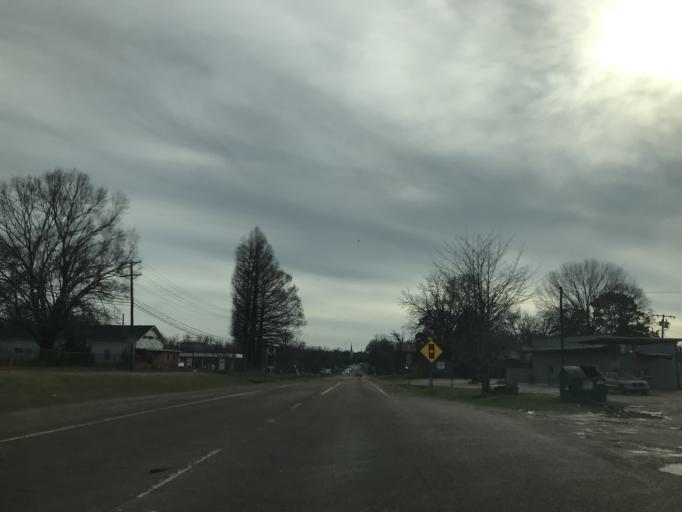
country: US
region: Mississippi
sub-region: Claiborne County
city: Port Gibson
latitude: 31.9706
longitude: -90.9784
